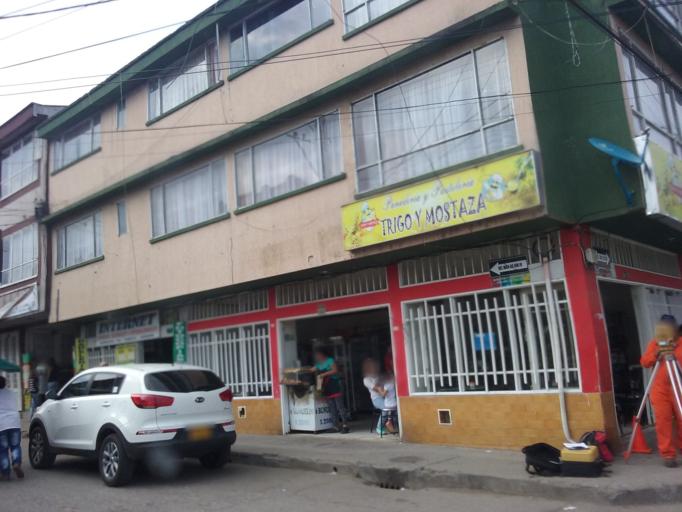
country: CO
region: Tolima
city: Libano
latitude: 4.9222
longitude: -75.0623
